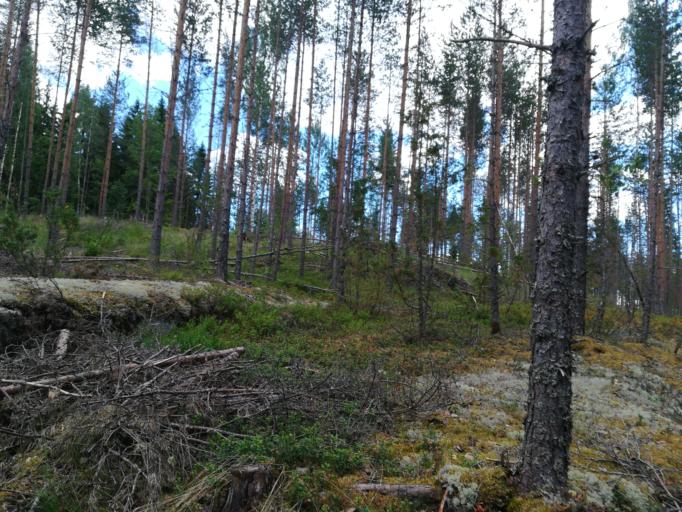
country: FI
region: Southern Savonia
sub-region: Mikkeli
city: Hirvensalmi
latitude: 61.7067
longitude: 26.9716
